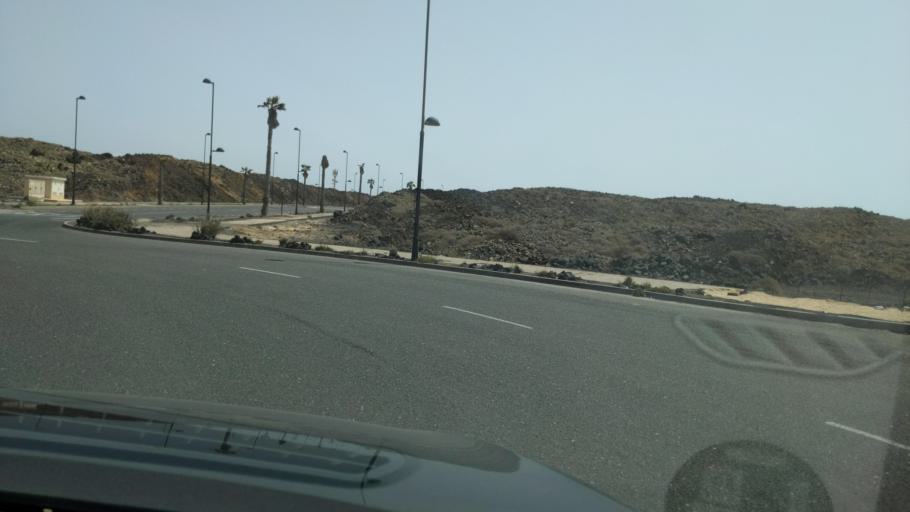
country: ES
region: Canary Islands
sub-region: Provincia de Las Palmas
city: Corralejo
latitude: 28.7372
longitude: -13.9449
